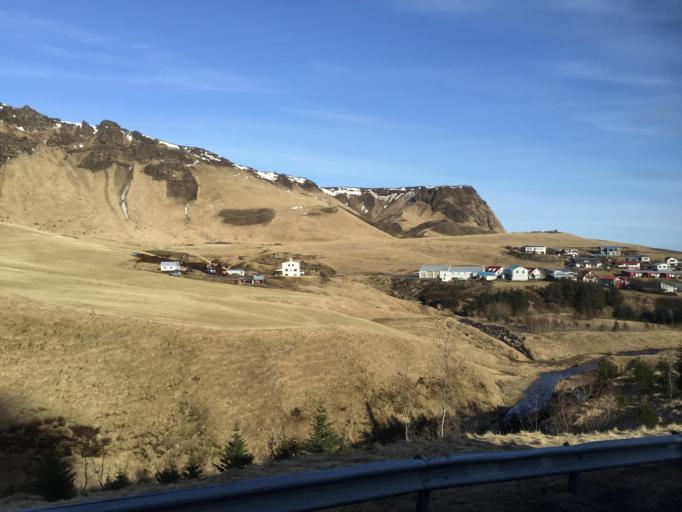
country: IS
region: South
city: Vestmannaeyjar
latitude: 63.4226
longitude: -19.0147
